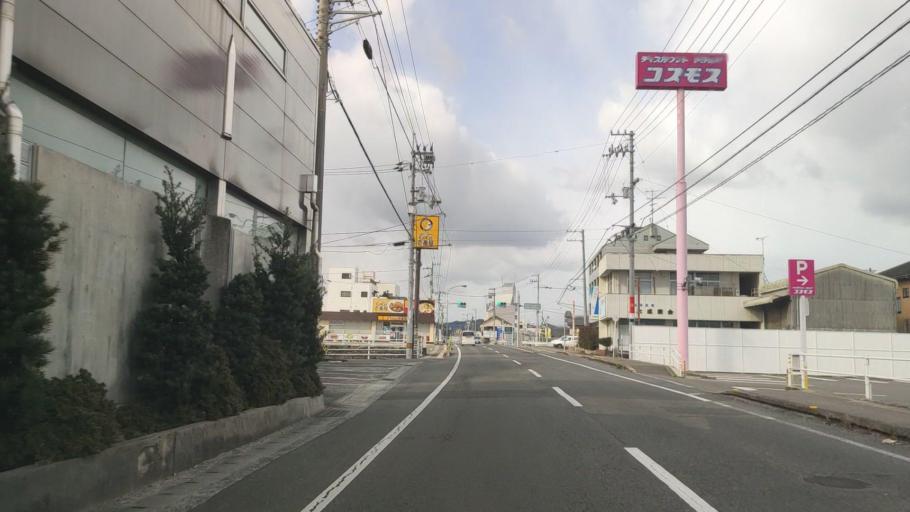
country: JP
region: Ehime
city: Saijo
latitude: 34.0474
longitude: 133.0184
